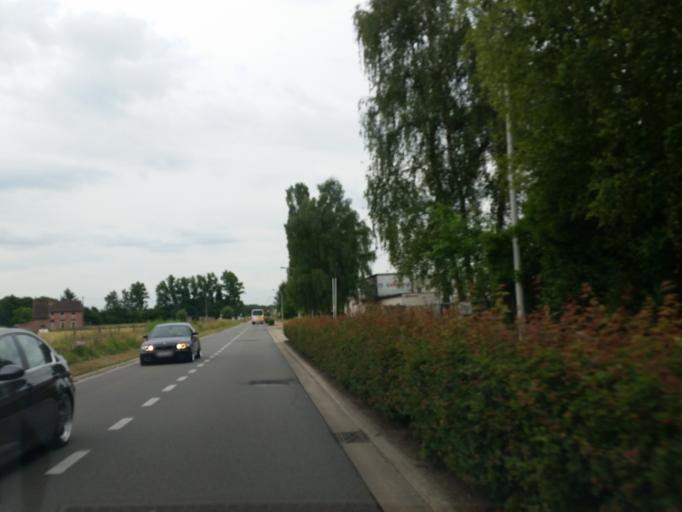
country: BE
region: Flanders
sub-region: Provincie Antwerpen
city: Ranst
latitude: 51.1665
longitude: 4.5929
